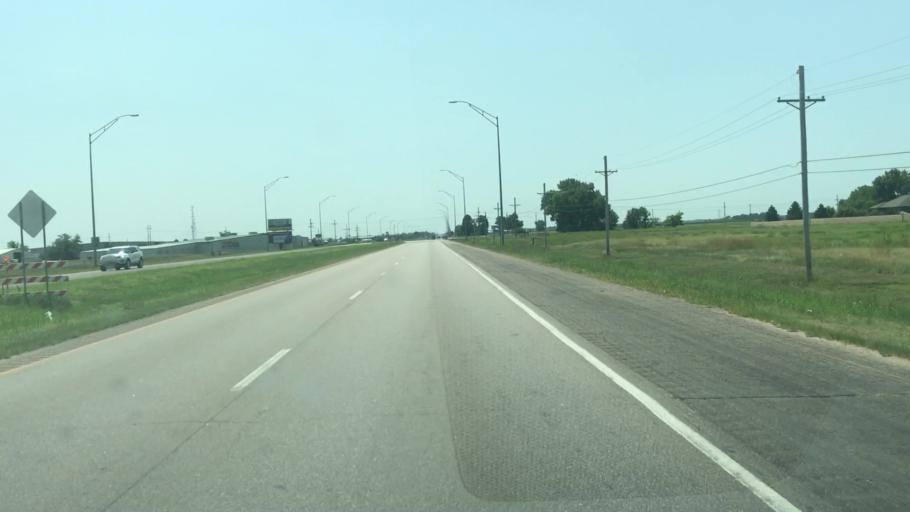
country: US
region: Nebraska
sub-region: Hall County
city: Grand Island
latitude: 40.8768
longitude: -98.3783
